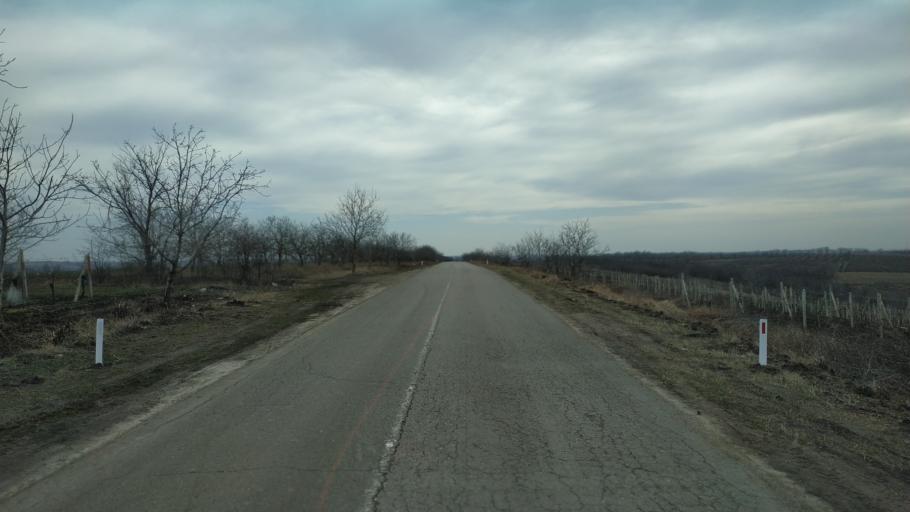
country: MD
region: Nisporeni
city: Nisporeni
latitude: 46.9514
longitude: 28.2385
